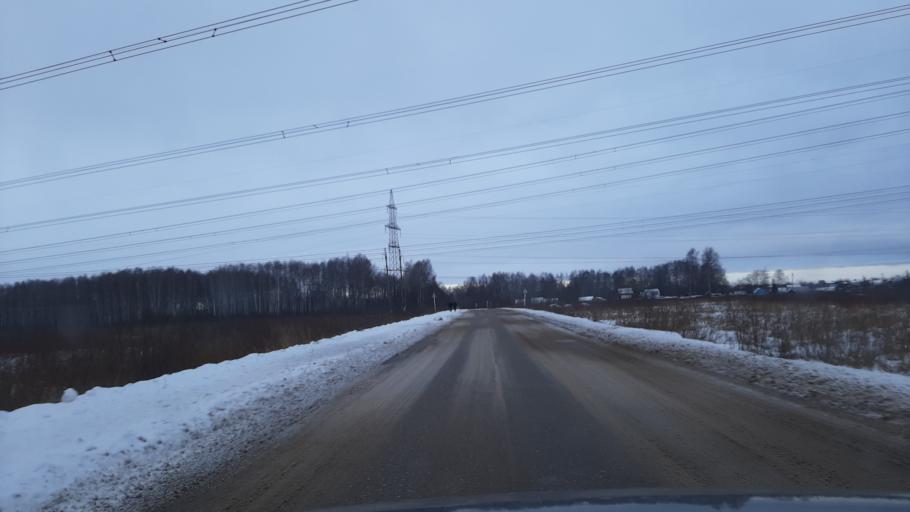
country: RU
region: Kostroma
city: Volgorechensk
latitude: 57.4442
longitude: 41.1409
